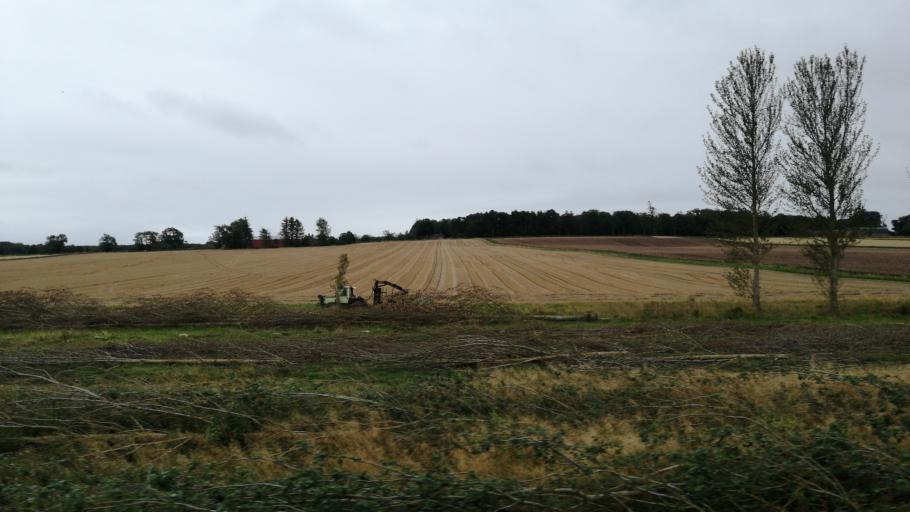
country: GB
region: Scotland
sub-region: Angus
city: Arbroath
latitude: 56.6057
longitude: -2.5822
